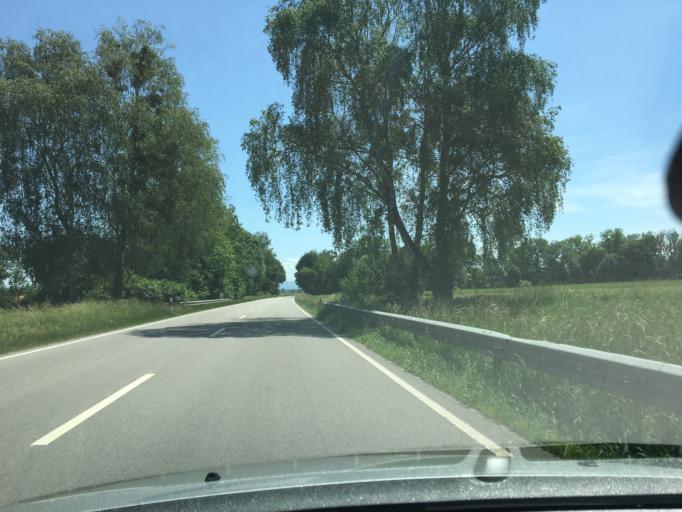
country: DE
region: Bavaria
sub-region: Upper Bavaria
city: Tittmoning
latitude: 48.0457
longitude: 12.7809
